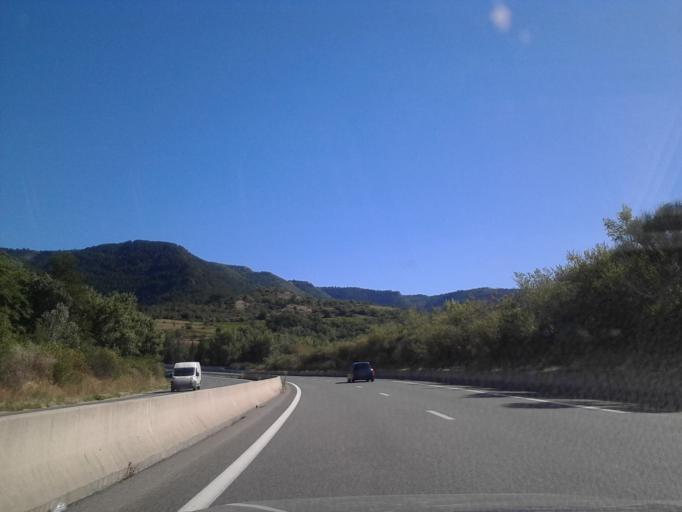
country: FR
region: Languedoc-Roussillon
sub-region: Departement de l'Herault
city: Lodeve
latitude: 43.7650
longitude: 3.3345
